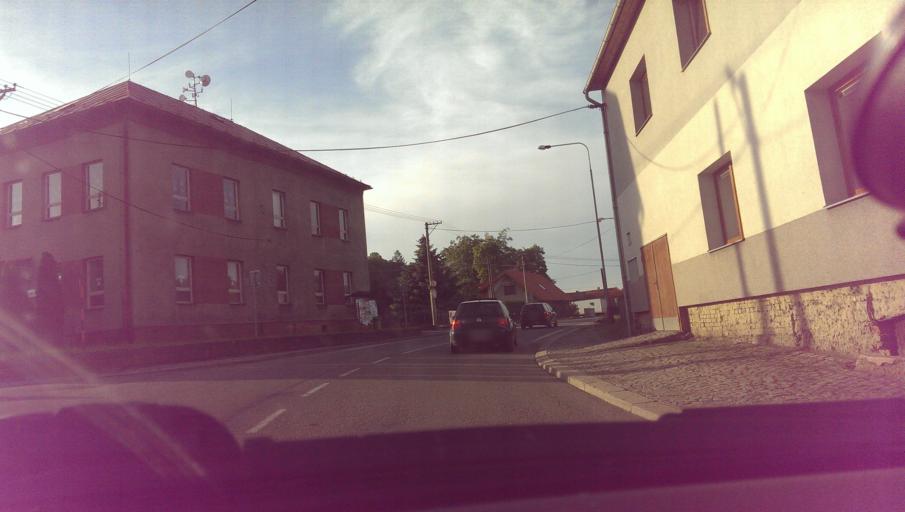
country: CZ
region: Zlin
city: Valasska Polanka
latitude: 49.2593
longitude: 17.9961
